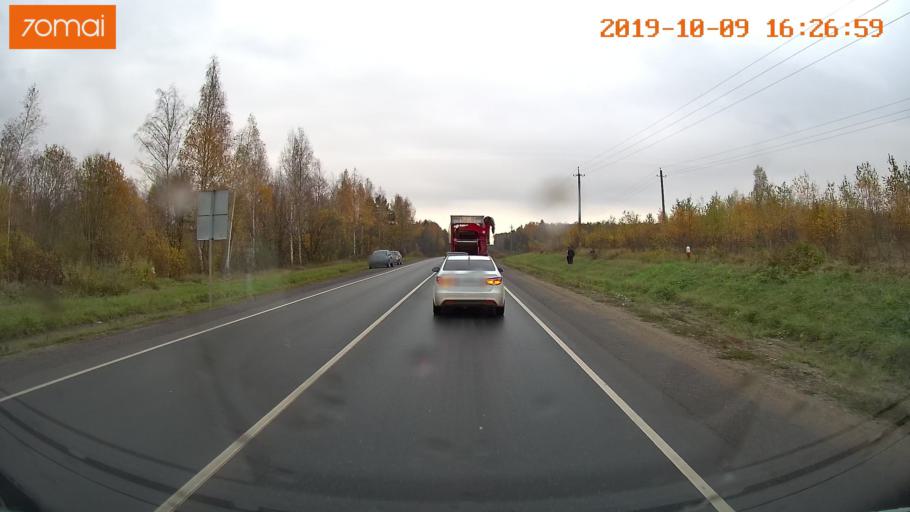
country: RU
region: Kostroma
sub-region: Kostromskoy Rayon
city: Kostroma
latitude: 57.6351
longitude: 40.9263
